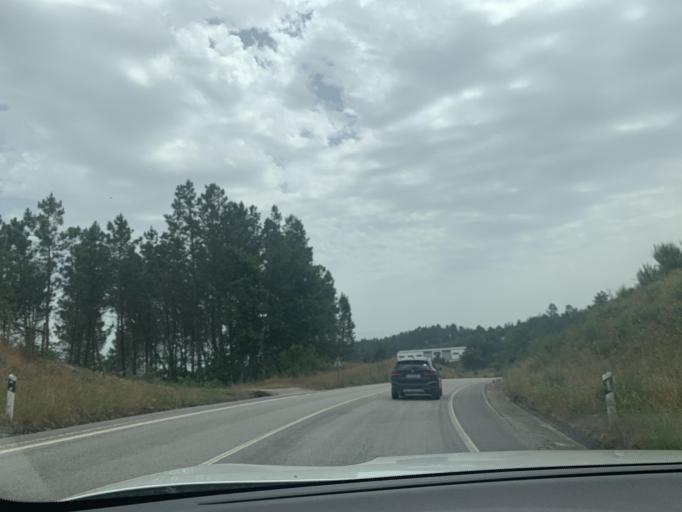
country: PT
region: Viseu
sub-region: Mangualde
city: Mangualde
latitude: 40.5667
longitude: -7.7223
